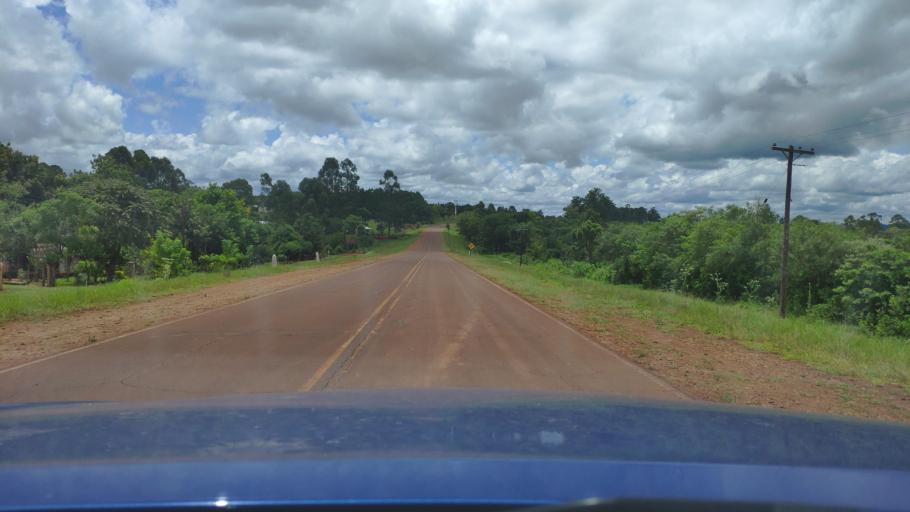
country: AR
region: Misiones
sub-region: Departamento de San Javier
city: San Javier
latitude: -27.8602
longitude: -55.2537
